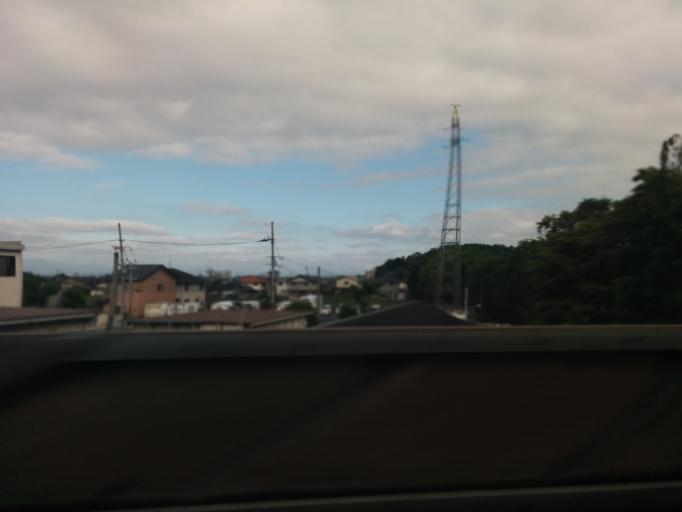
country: JP
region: Shiga Prefecture
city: Hikone
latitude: 35.2449
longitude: 136.2696
